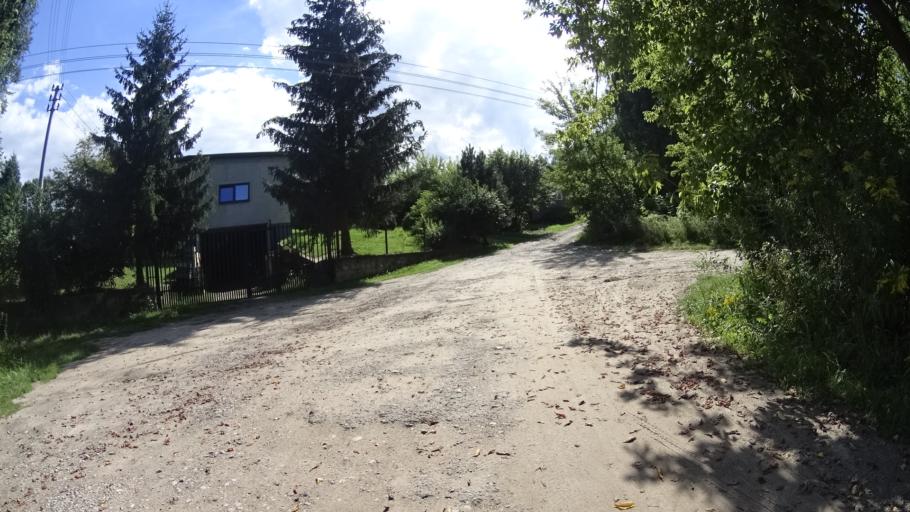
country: PL
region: Masovian Voivodeship
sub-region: Powiat grojecki
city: Mogielnica
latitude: 51.6941
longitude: 20.7125
